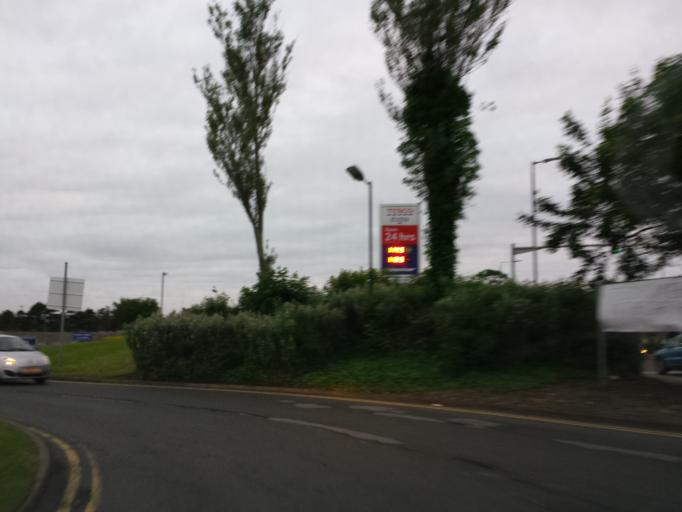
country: GB
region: Scotland
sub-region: South Ayrshire
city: Prestwick
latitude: 55.4688
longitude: -4.6089
